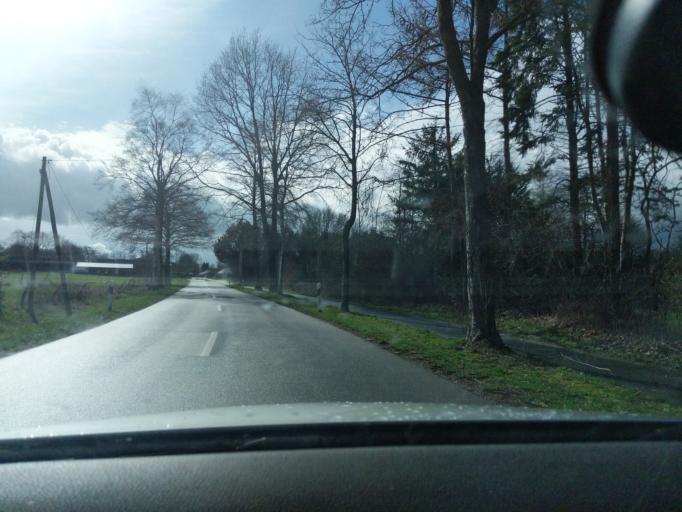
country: DE
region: Lower Saxony
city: Kranenburg
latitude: 53.6068
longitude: 9.2133
